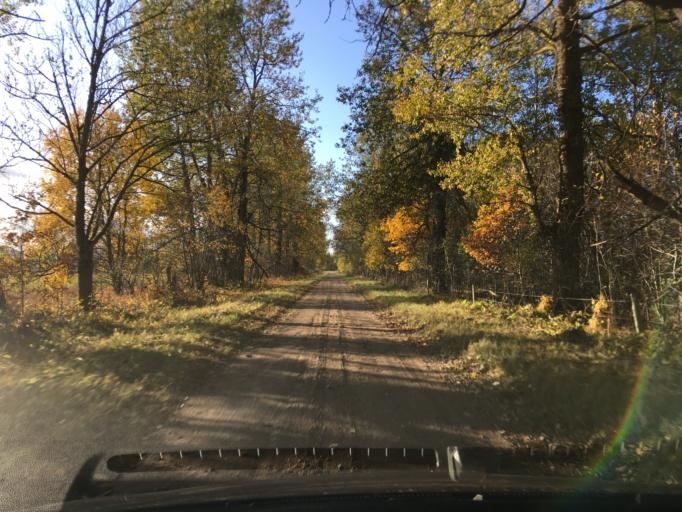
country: EE
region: Laeaene
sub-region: Lihula vald
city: Lihula
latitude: 58.5646
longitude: 23.7925
